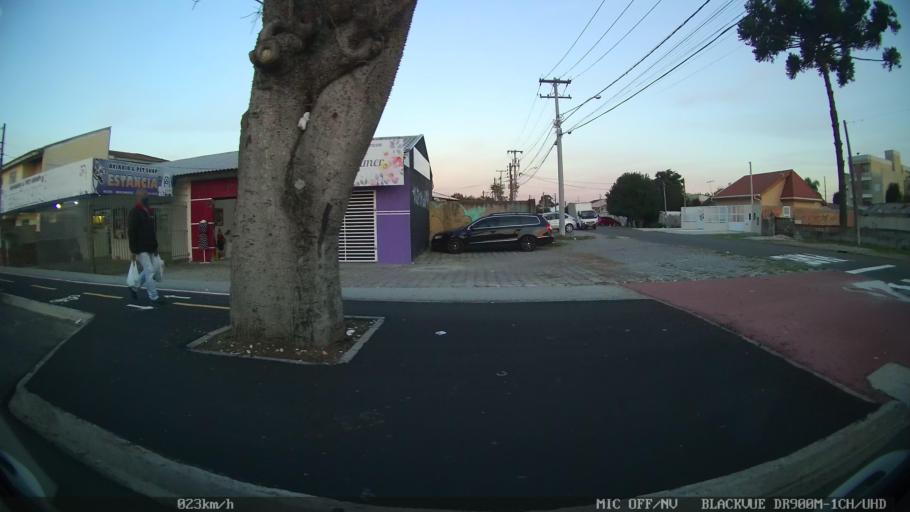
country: BR
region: Parana
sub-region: Pinhais
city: Pinhais
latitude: -25.4420
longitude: -49.1980
